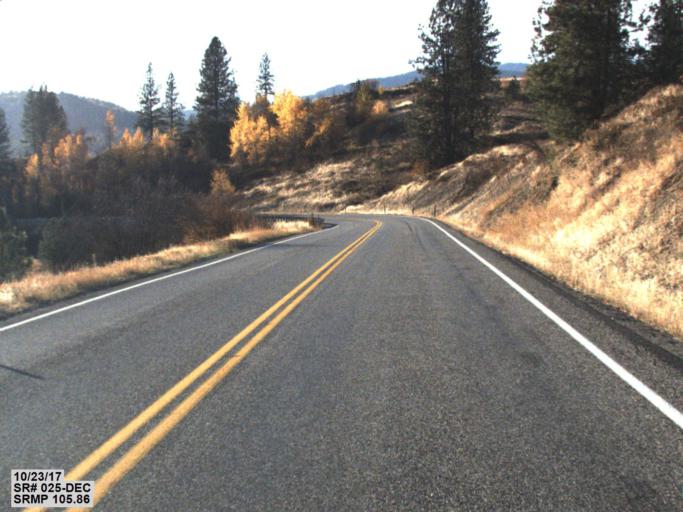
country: CA
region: British Columbia
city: Rossland
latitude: 48.8512
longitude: -117.8931
